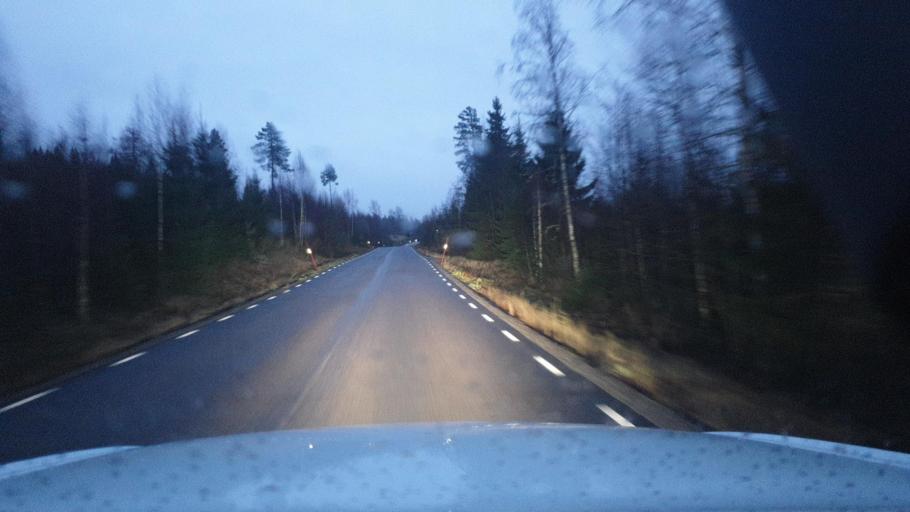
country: SE
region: Vaermland
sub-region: Torsby Kommun
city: Torsby
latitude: 59.9902
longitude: 12.7488
